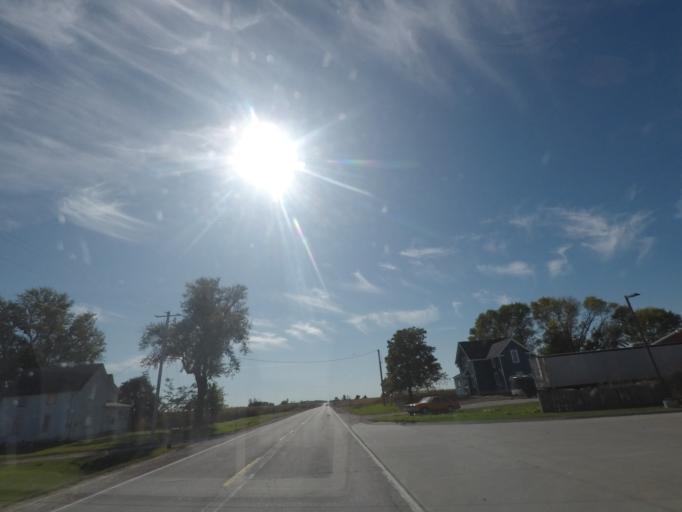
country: US
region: Iowa
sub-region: Story County
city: Nevada
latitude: 42.0148
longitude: -93.3095
